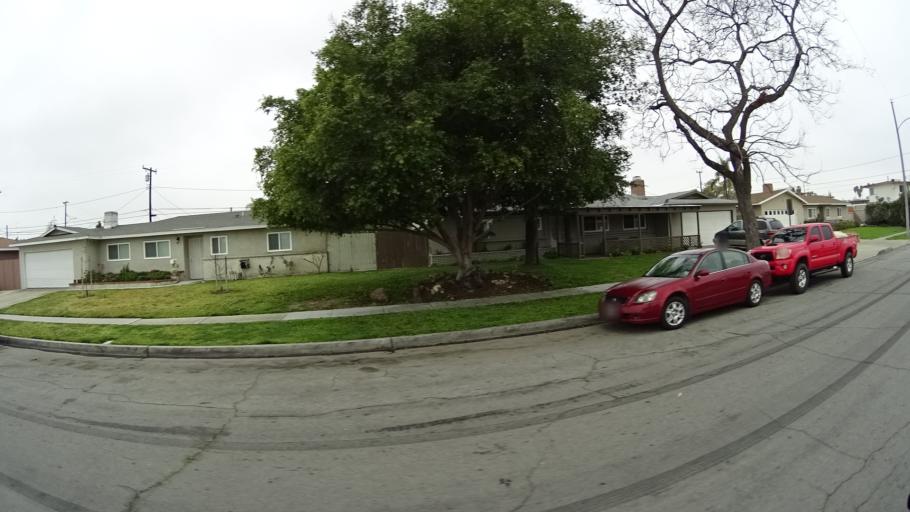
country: US
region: California
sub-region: Orange County
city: Stanton
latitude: 33.8260
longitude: -118.0082
